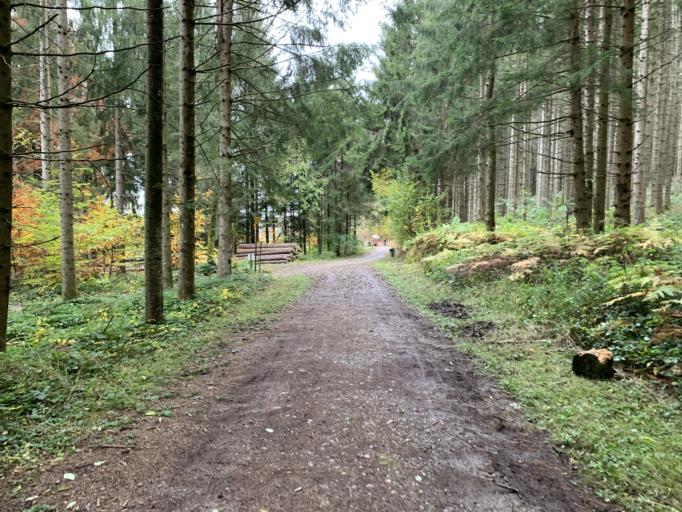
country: CH
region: Zurich
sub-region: Bezirk Hinwil
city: Baretswil
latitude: 47.3569
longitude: 8.8500
